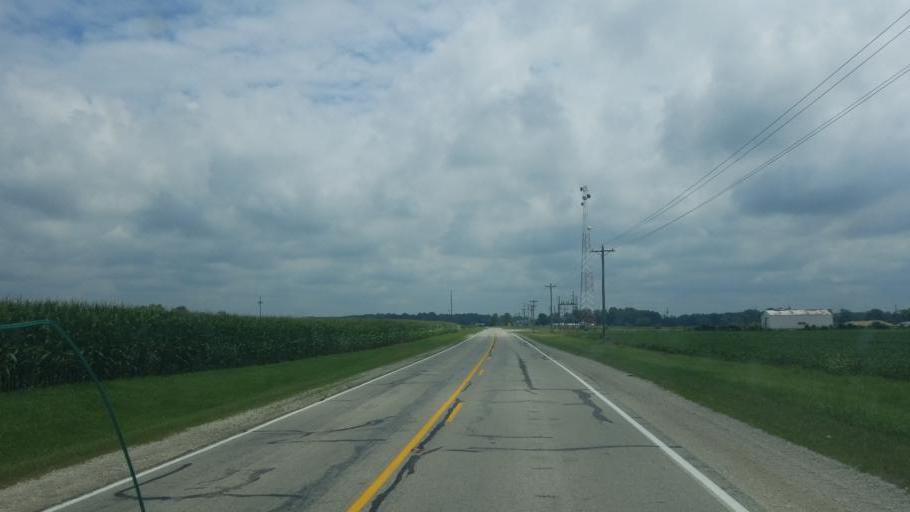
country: US
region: Indiana
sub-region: Huntington County
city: Warren
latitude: 40.6682
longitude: -85.4431
